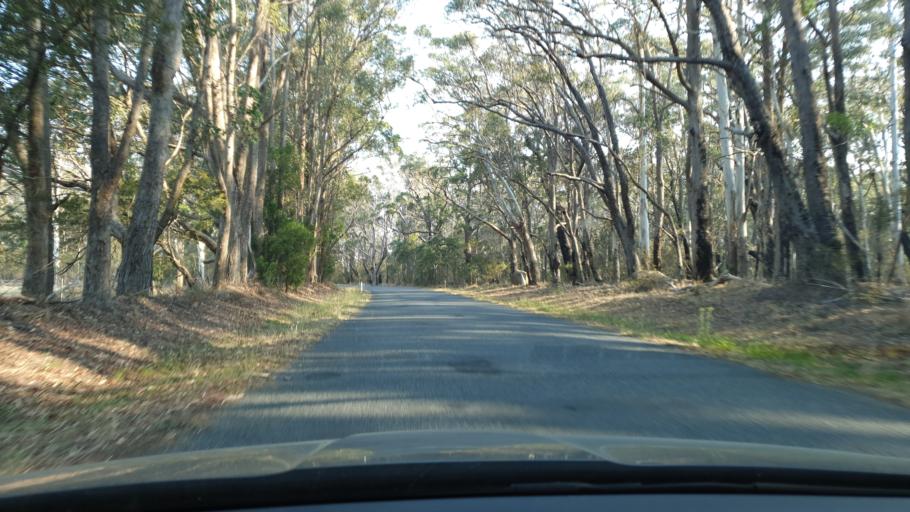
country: AU
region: New South Wales
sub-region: Tenterfield Municipality
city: Carrolls Creek
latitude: -28.6946
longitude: 152.0908
